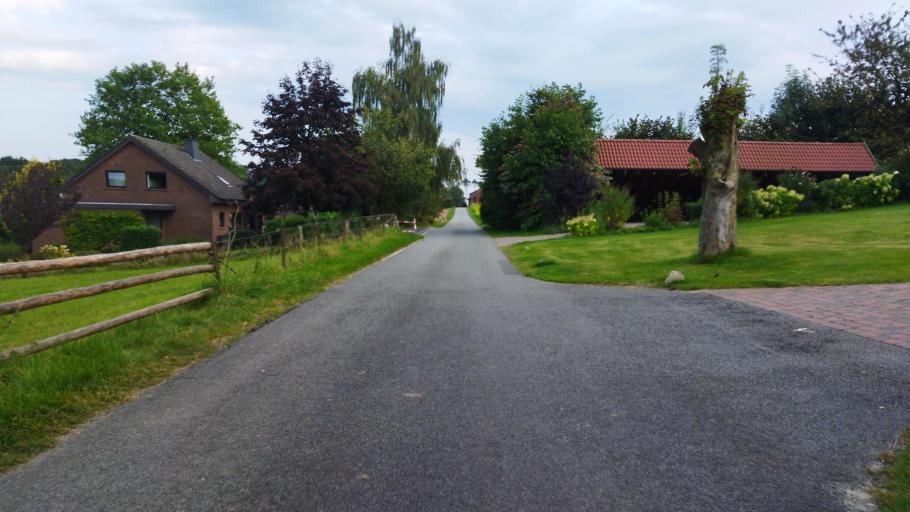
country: DE
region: Lower Saxony
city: Bad Iburg
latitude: 52.1749
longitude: 8.0130
